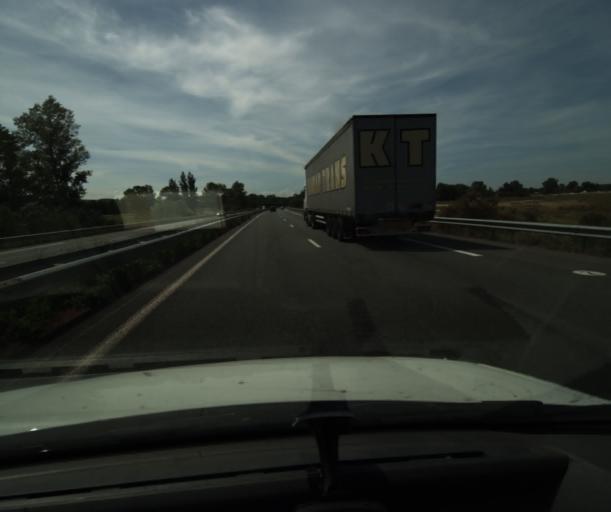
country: FR
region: Languedoc-Roussillon
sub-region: Departement de l'Aude
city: Castelnaudary
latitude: 43.2861
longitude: 1.9560
